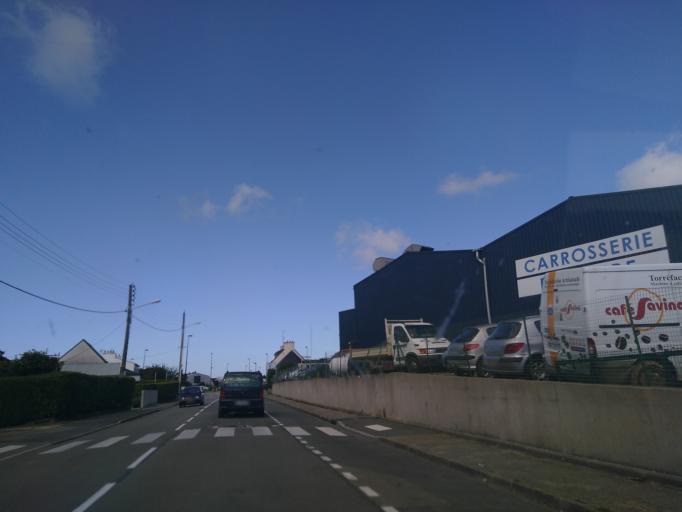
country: FR
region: Brittany
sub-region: Departement du Finistere
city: Crozon
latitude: 48.2468
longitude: -4.4982
